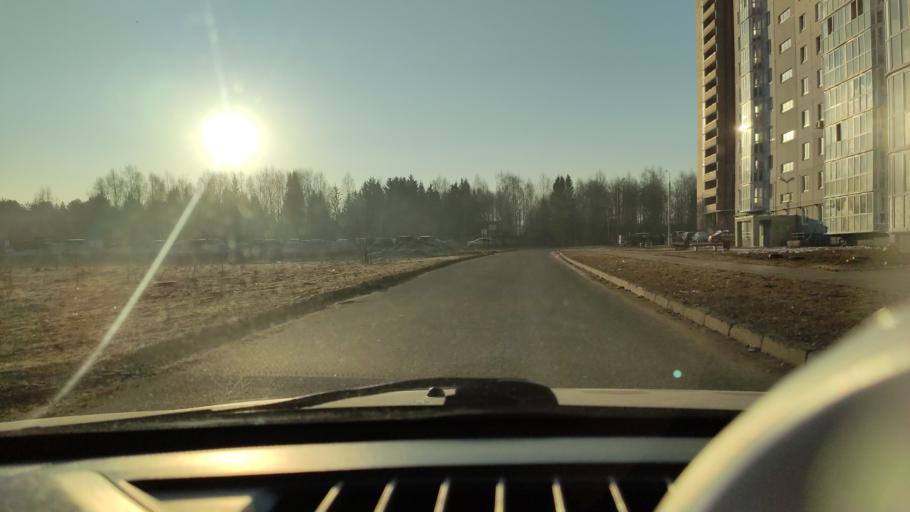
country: RU
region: Perm
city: Polazna
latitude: 58.1364
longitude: 56.3979
